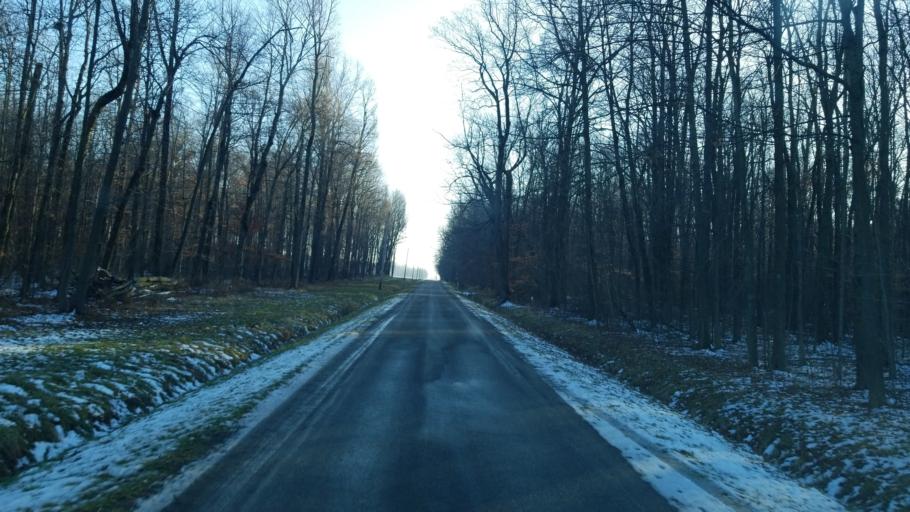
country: US
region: Ohio
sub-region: Crawford County
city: Bucyrus
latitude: 40.9265
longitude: -82.9210
